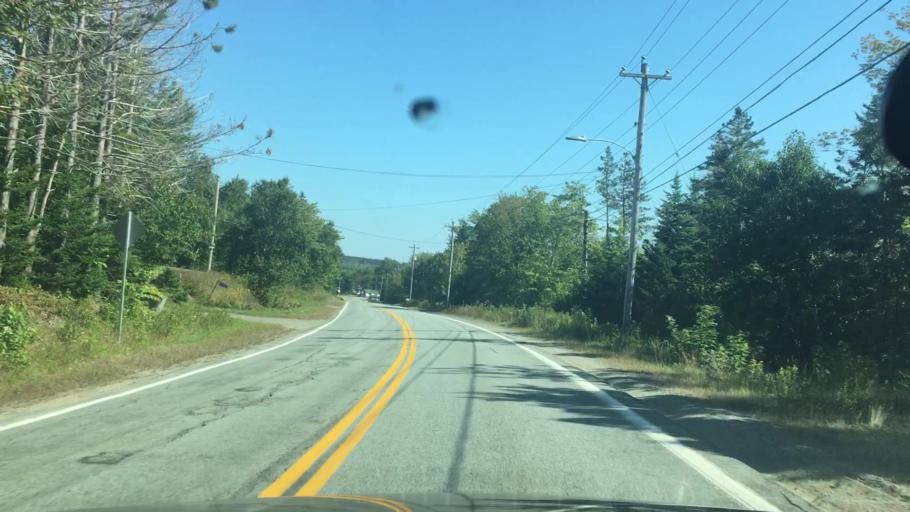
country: CA
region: Nova Scotia
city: New Glasgow
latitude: 44.9109
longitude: -62.5426
